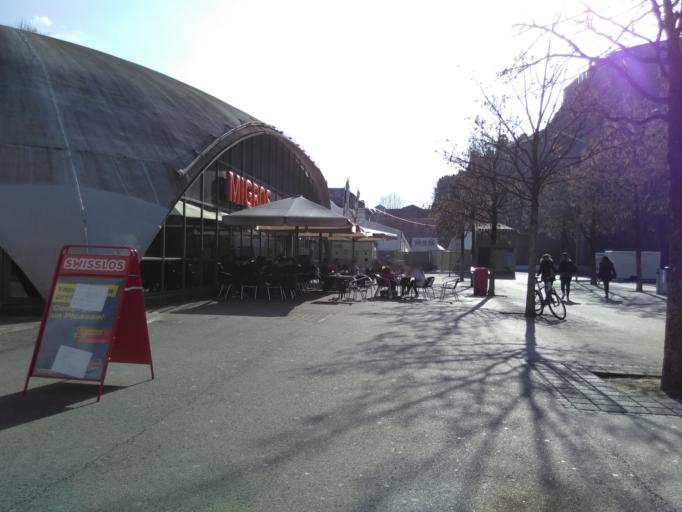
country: CH
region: Ticino
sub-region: Bellinzona District
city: Bellinzona
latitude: 46.1940
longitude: 9.0241
